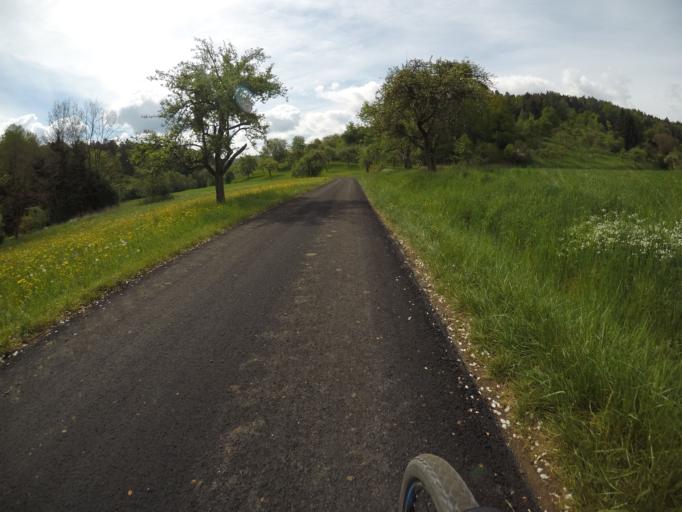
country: DE
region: Baden-Wuerttemberg
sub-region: Tuebingen Region
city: Tuebingen
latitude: 48.5317
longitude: 9.0055
